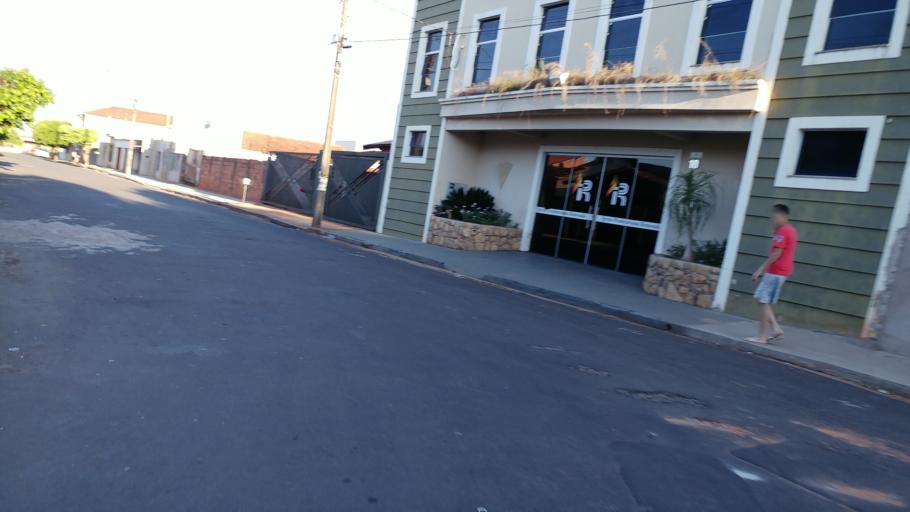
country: BR
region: Sao Paulo
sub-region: Paraguacu Paulista
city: Paraguacu Paulista
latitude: -22.4315
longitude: -50.5843
